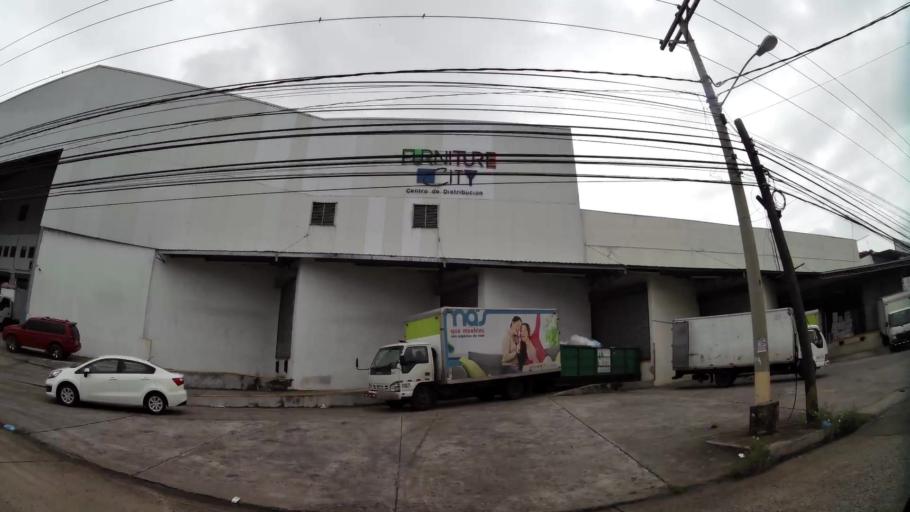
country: PA
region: Panama
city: Panama
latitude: 9.0024
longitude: -79.5269
